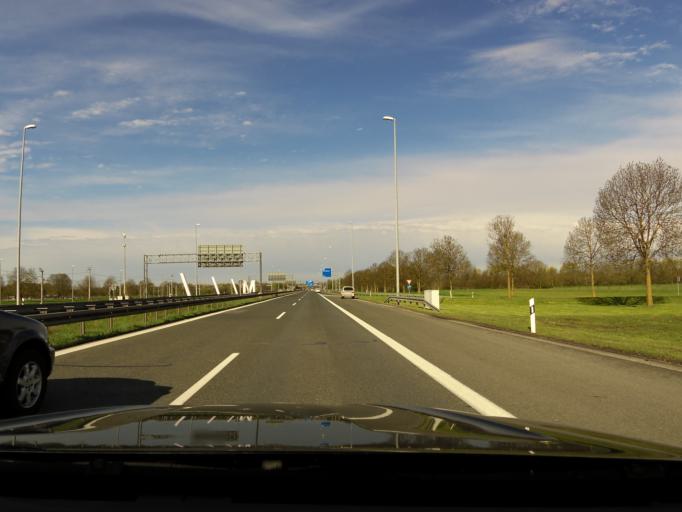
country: DE
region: Bavaria
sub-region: Upper Bavaria
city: Hallbergmoos
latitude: 48.3517
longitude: 11.7501
